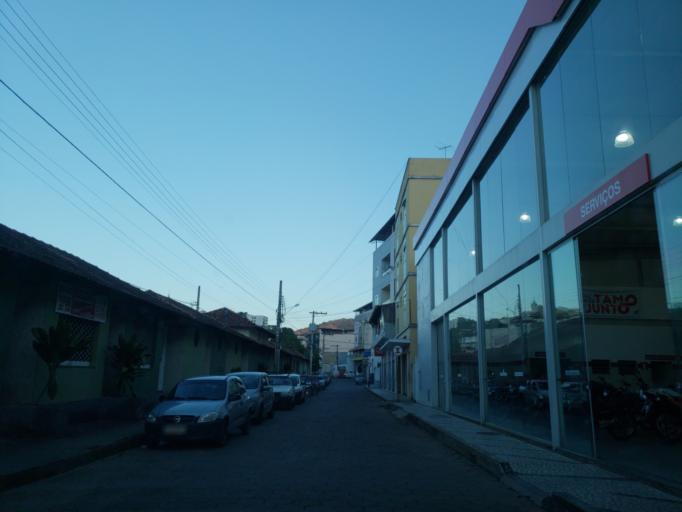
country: BR
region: Minas Gerais
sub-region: Sao Joao Nepomuceno
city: Sao Joao Nepomuceno
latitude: -21.5376
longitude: -43.0138
